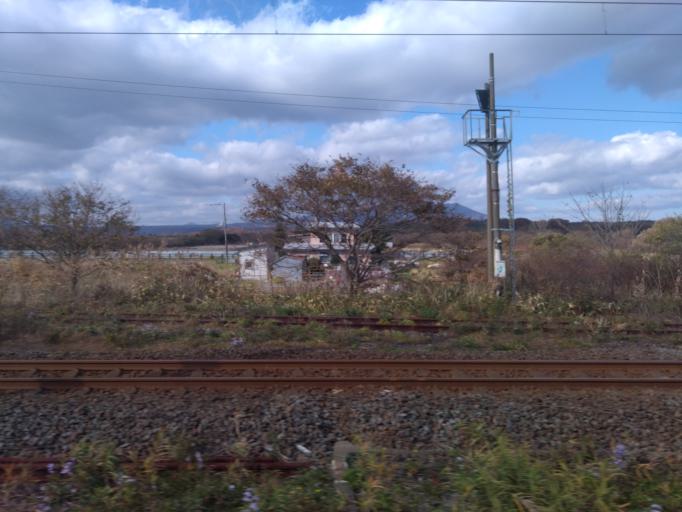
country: JP
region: Hokkaido
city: Shiraoi
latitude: 42.5800
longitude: 141.4206
